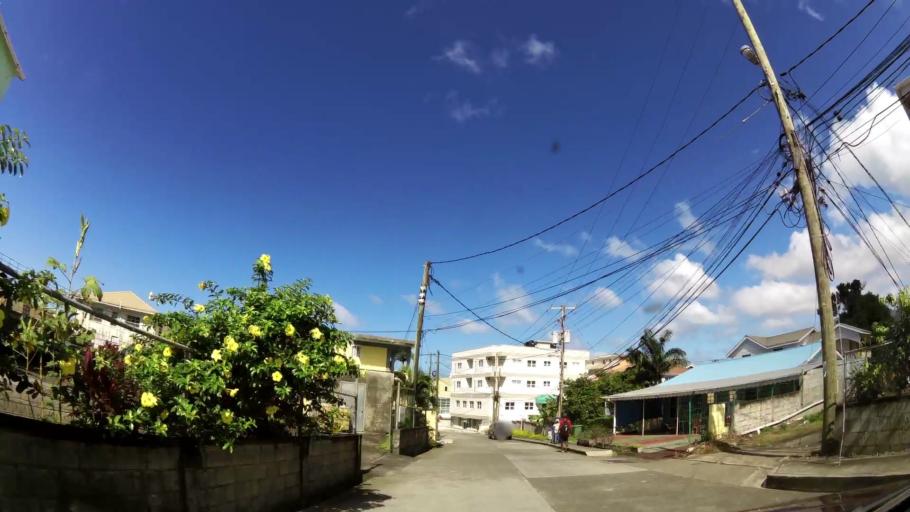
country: DM
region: Saint John
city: Portsmouth
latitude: 15.5555
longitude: -61.4580
